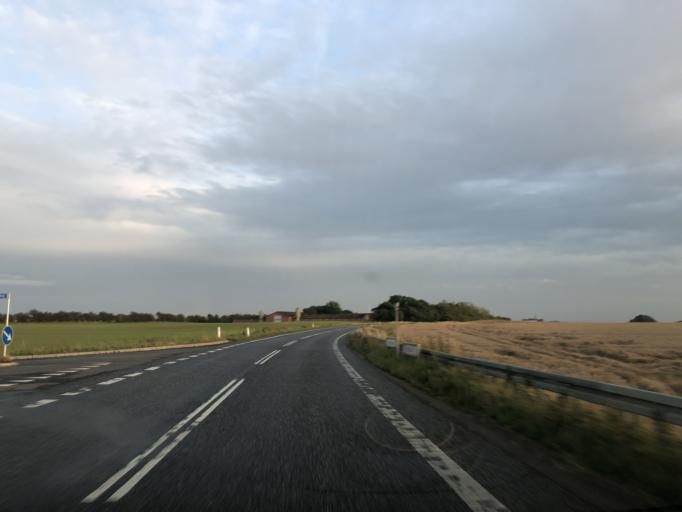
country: DK
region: Central Jutland
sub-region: Holstebro Kommune
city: Vinderup
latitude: 56.5930
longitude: 8.8834
